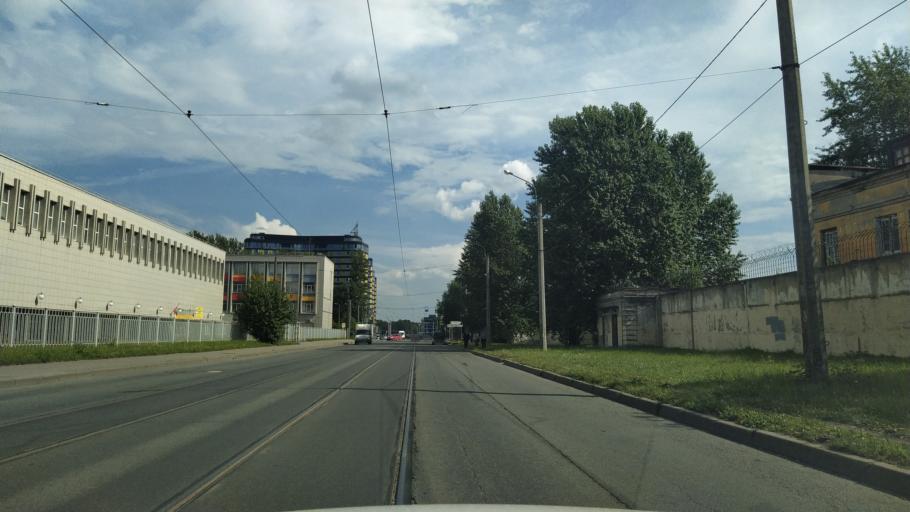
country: RU
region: Leningrad
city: Finlyandskiy
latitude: 59.9643
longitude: 30.3958
